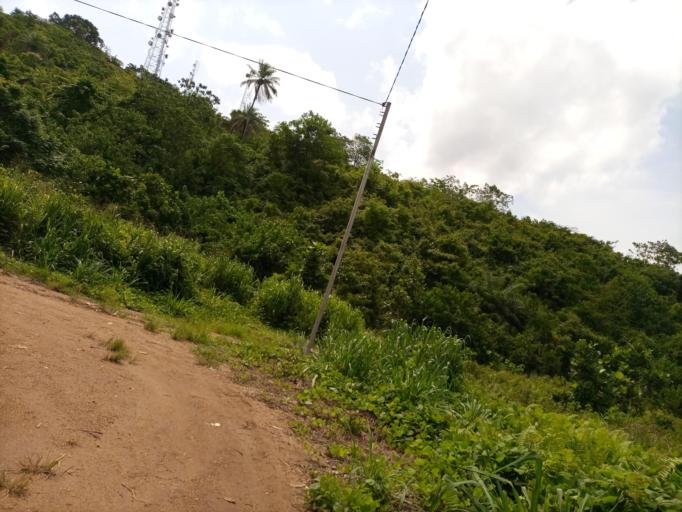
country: SL
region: Southern Province
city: Bo
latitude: 7.9758
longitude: -11.7581
